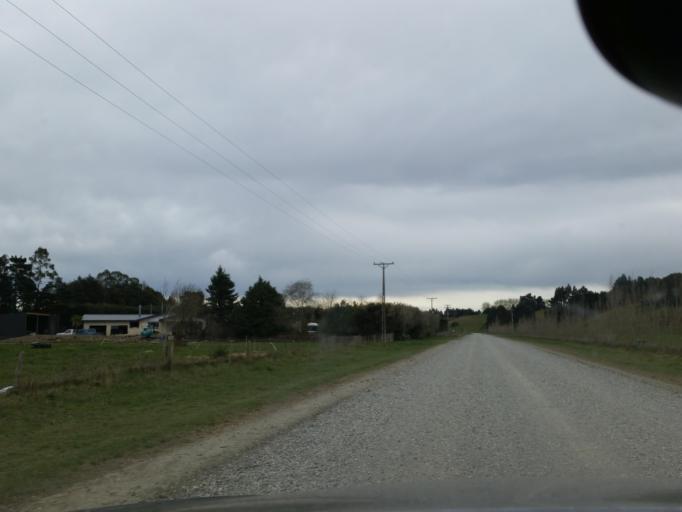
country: NZ
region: Southland
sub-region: Gore District
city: Gore
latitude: -45.8056
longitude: 168.6812
